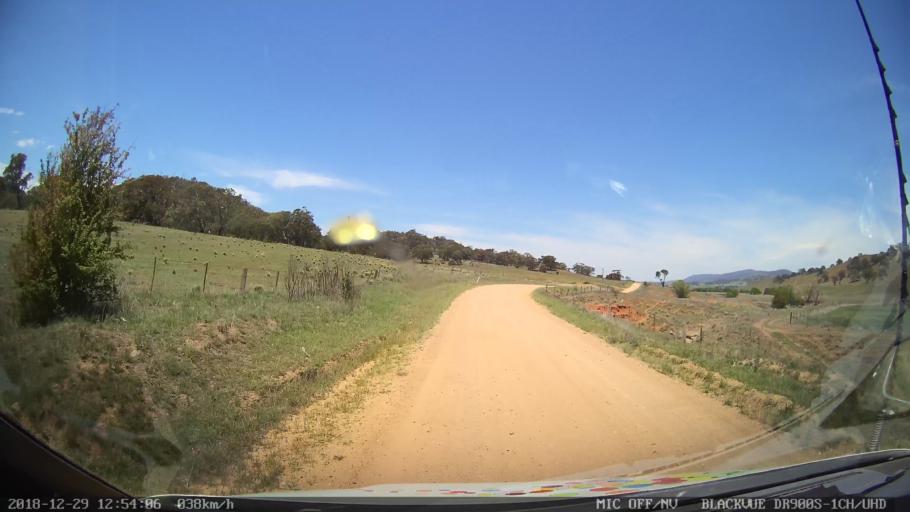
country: AU
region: Australian Capital Territory
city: Macarthur
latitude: -35.6894
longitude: 149.1875
